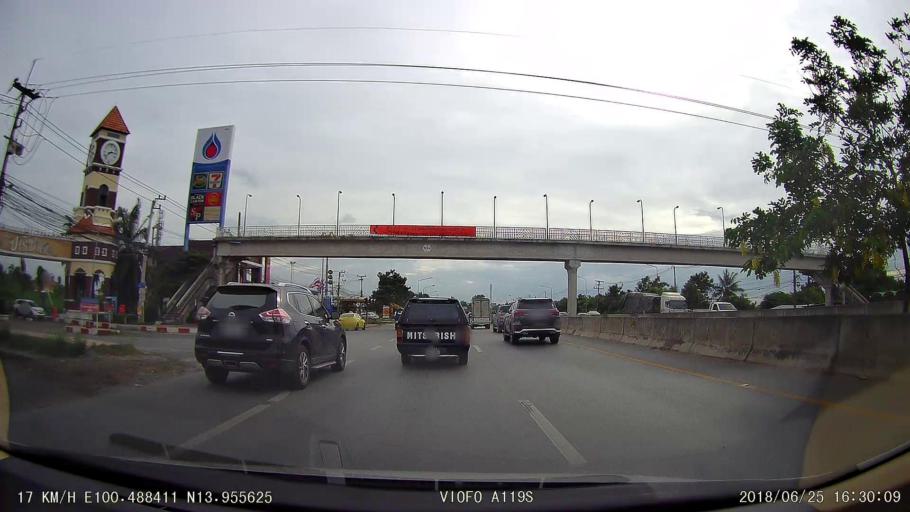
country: TH
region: Nonthaburi
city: Pak Kret
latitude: 13.9556
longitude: 100.4884
